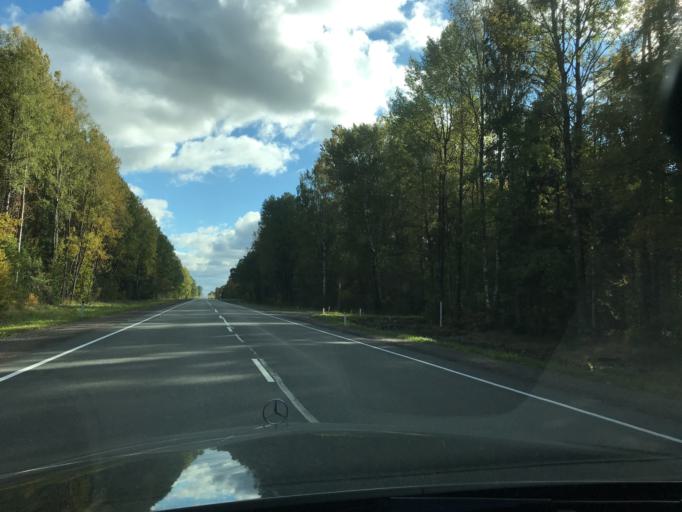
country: RU
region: Pskov
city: Ostrov
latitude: 57.1409
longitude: 28.5111
